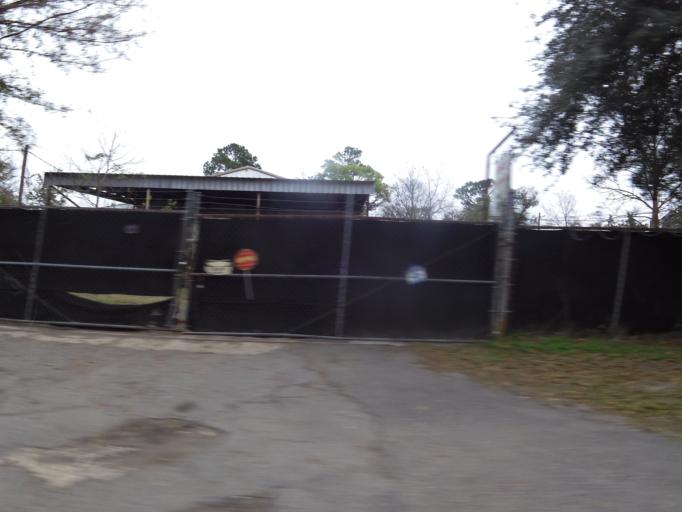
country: US
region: Florida
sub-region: Duval County
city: Jacksonville
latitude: 30.3624
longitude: -81.6972
